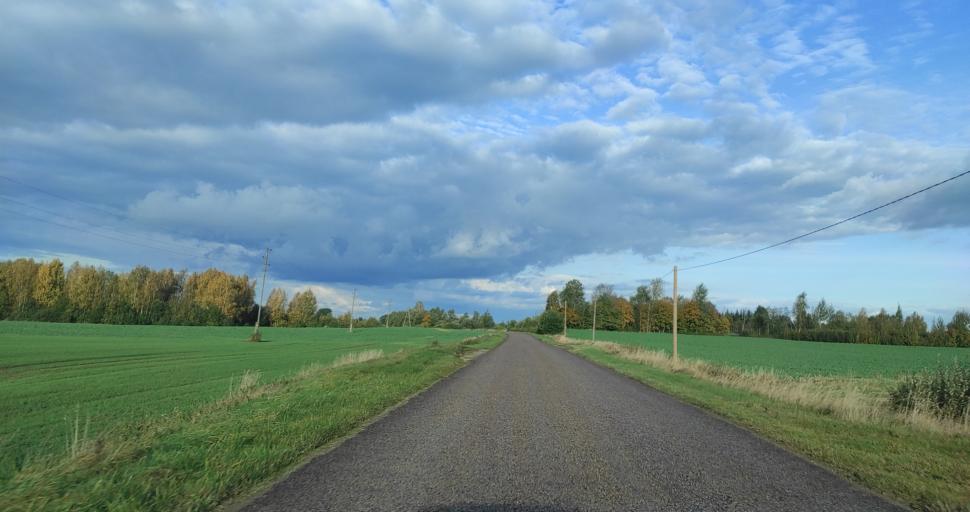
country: LV
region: Aizpute
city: Aizpute
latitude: 56.7784
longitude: 21.7771
